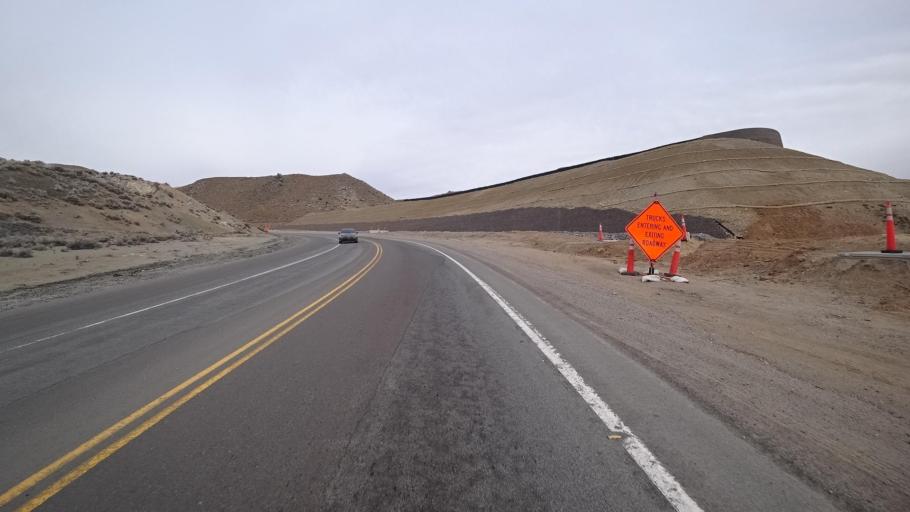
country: US
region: Nevada
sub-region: Washoe County
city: Sun Valley
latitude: 39.6108
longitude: -119.7344
